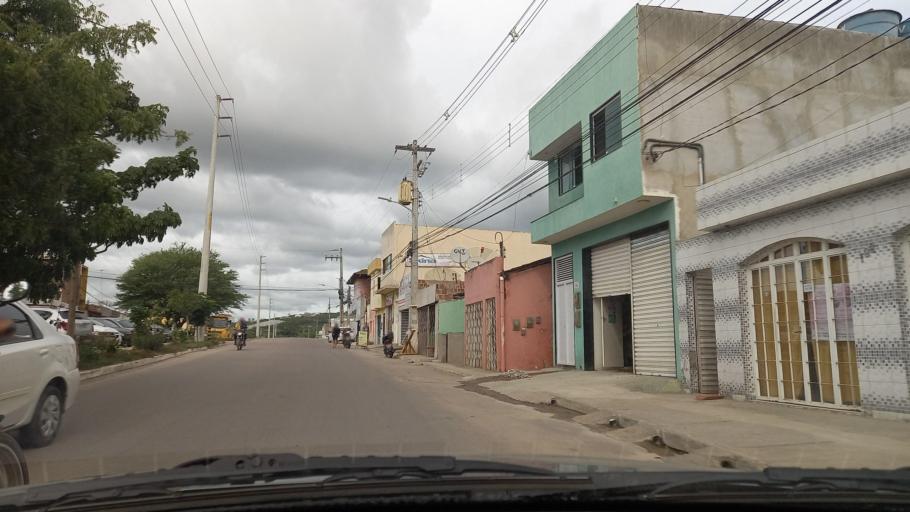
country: BR
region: Pernambuco
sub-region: Gravata
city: Gravata
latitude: -8.2054
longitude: -35.5636
